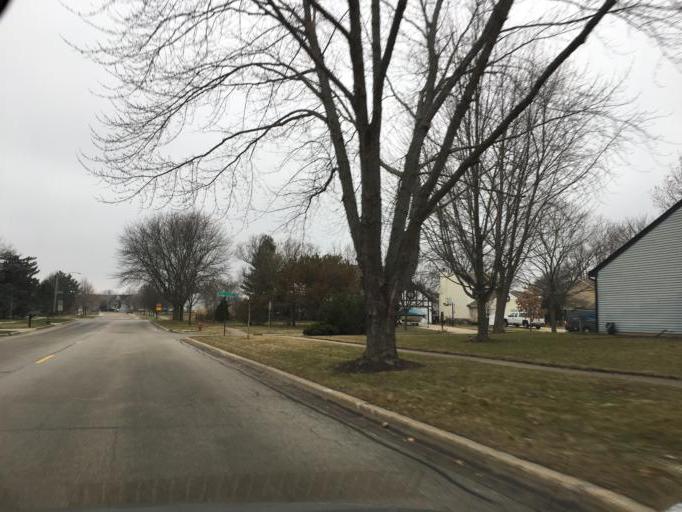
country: US
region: Illinois
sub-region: McHenry County
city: Lakewood
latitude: 42.2168
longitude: -88.3631
